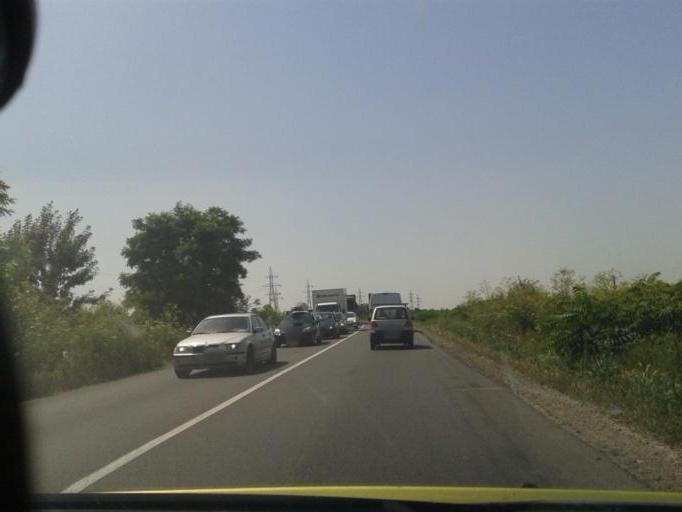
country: RO
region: Ilfov
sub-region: Comuna Glina
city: Catelu
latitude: 44.4277
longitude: 26.2350
